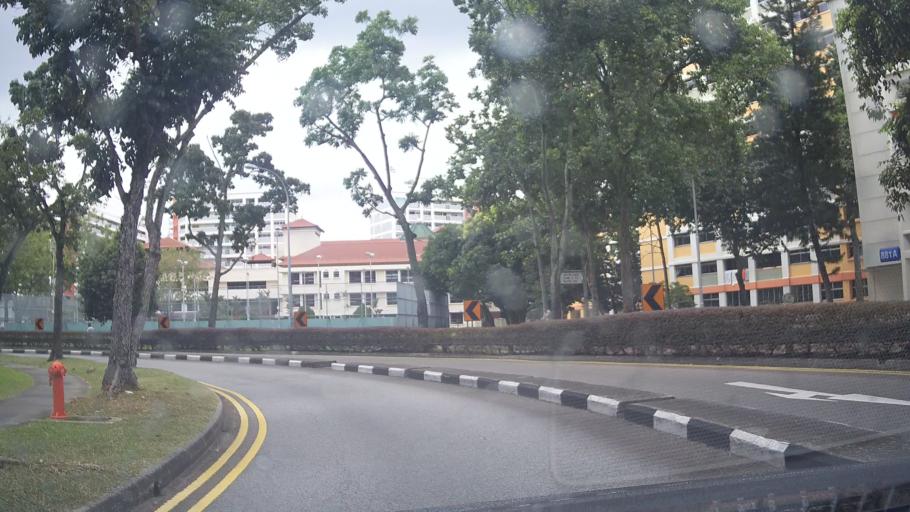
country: MY
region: Johor
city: Johor Bahru
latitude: 1.4440
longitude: 103.7917
